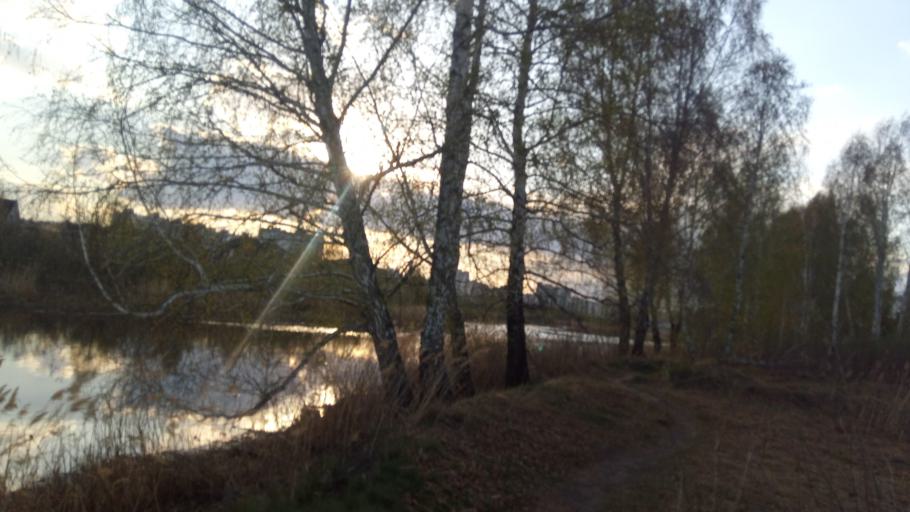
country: RU
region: Chelyabinsk
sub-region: Gorod Chelyabinsk
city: Chelyabinsk
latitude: 55.1586
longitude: 61.3180
